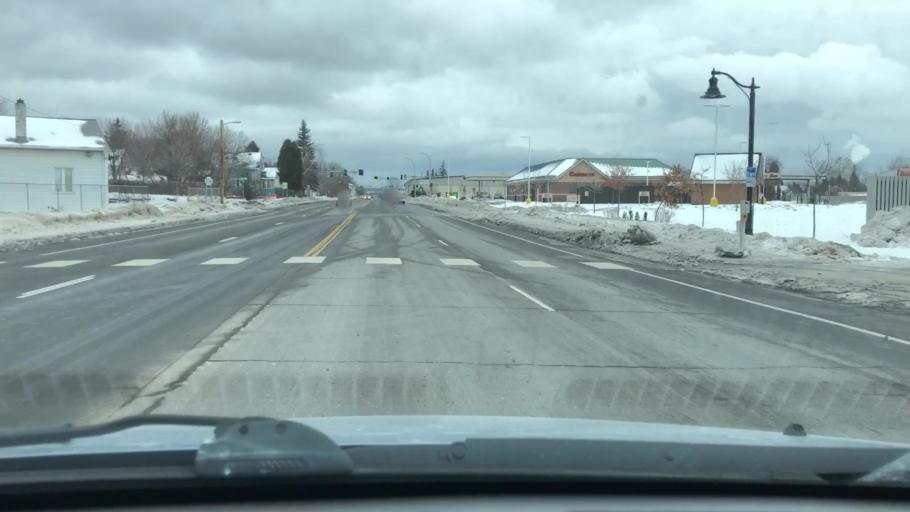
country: US
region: Minnesota
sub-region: Saint Louis County
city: Proctor
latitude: 46.7300
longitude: -92.1819
